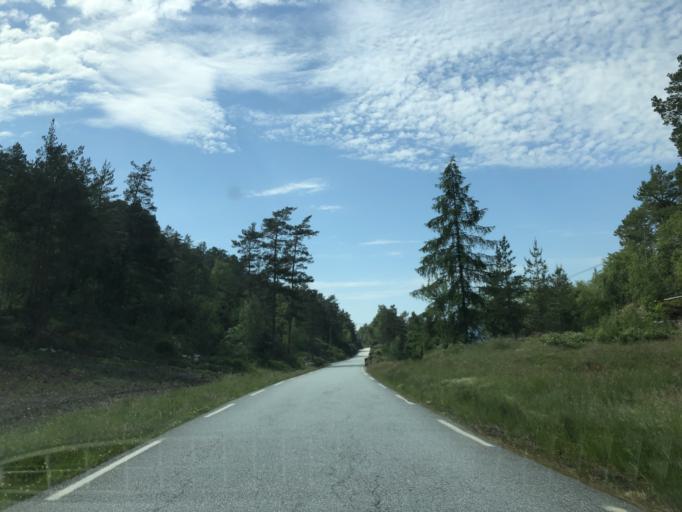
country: NO
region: Hordaland
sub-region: Jondal
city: Jondal
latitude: 60.3242
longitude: 6.3363
